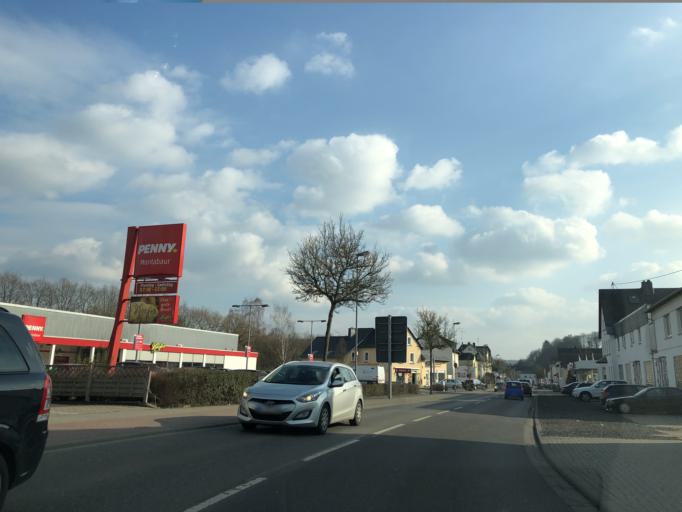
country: DE
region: Rheinland-Pfalz
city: Montabaur
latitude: 50.4396
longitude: 7.8312
